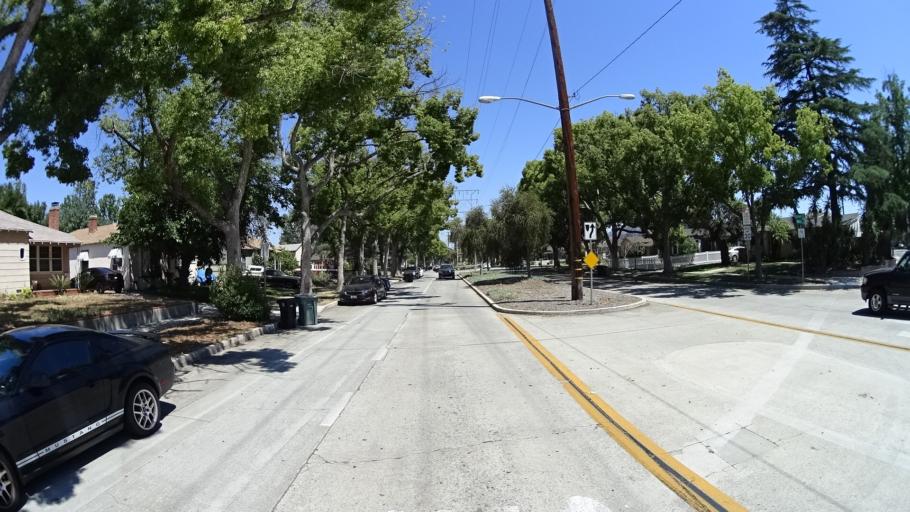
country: US
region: California
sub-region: Los Angeles County
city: North Hollywood
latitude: 34.1794
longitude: -118.3575
